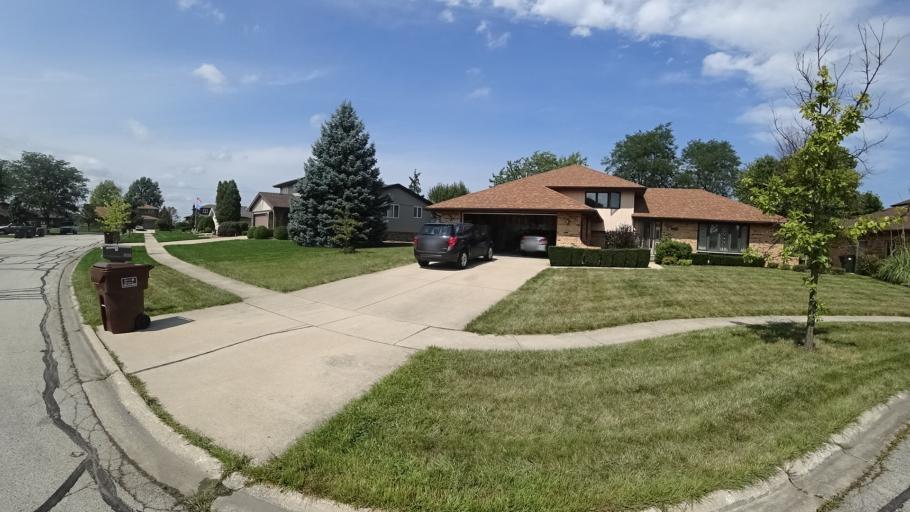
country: US
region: Illinois
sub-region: Cook County
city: Tinley Park
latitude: 41.5698
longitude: -87.8149
